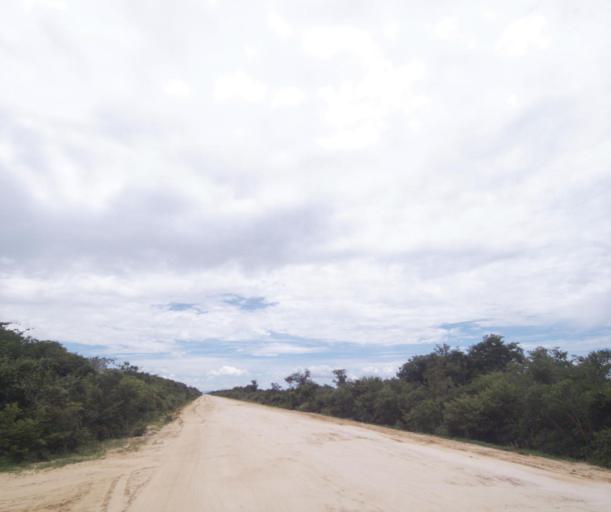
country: BR
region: Bahia
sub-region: Carinhanha
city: Carinhanha
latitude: -14.2411
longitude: -43.8500
